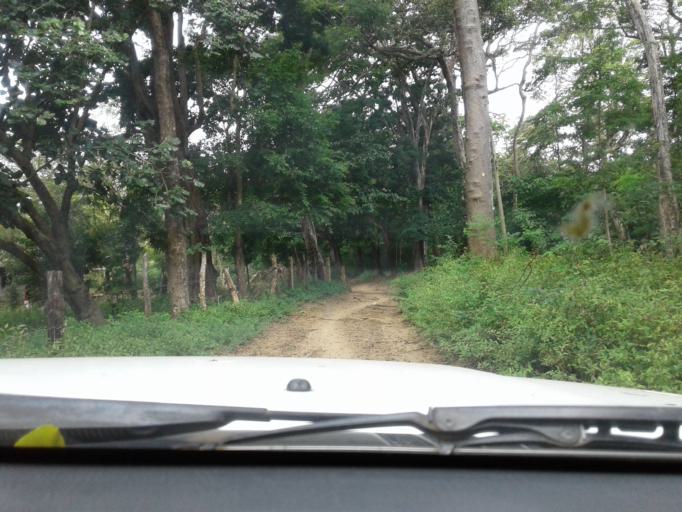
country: NI
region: Rivas
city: San Juan del Sur
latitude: 11.2234
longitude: -85.7865
